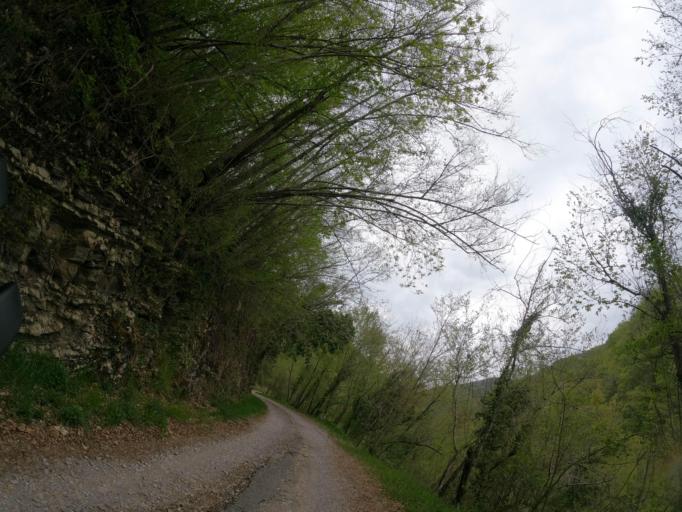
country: IT
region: Friuli Venezia Giulia
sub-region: Provincia di Udine
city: Stregna
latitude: 46.1191
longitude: 13.6124
